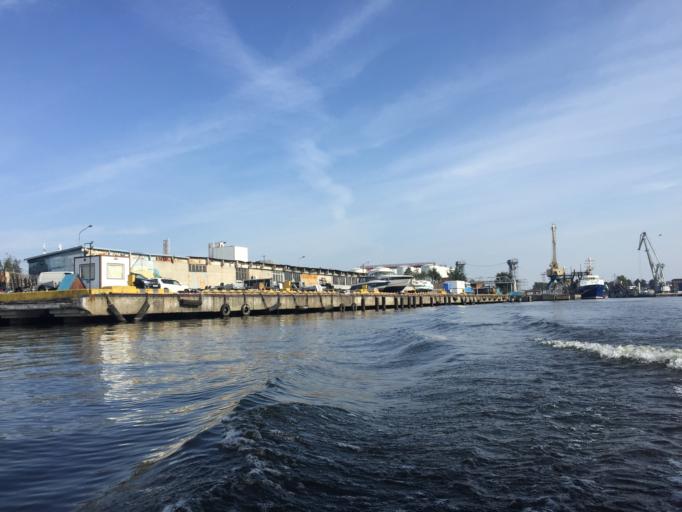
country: RU
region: Kaliningrad
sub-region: Gorod Kaliningrad
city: Kaliningrad
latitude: 54.7046
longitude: 20.4780
